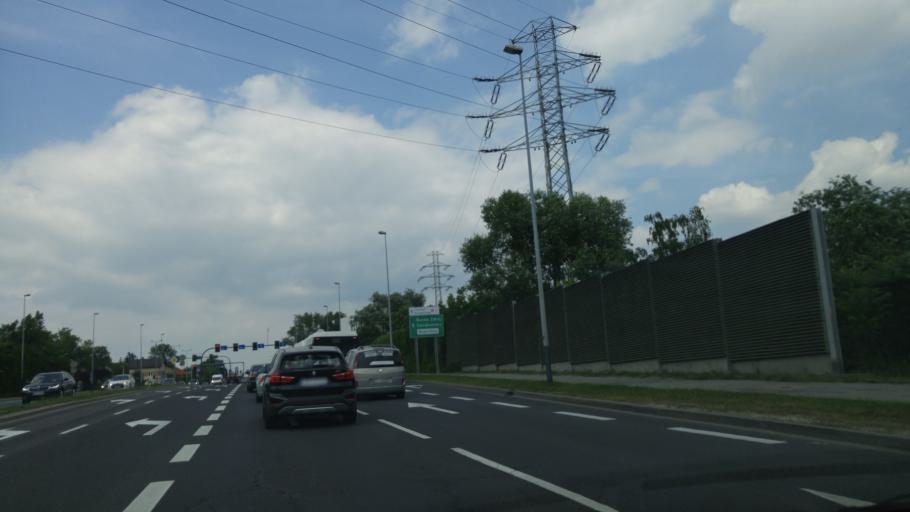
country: PL
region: Lesser Poland Voivodeship
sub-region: Krakow
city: Krakow
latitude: 50.0136
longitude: 19.9454
